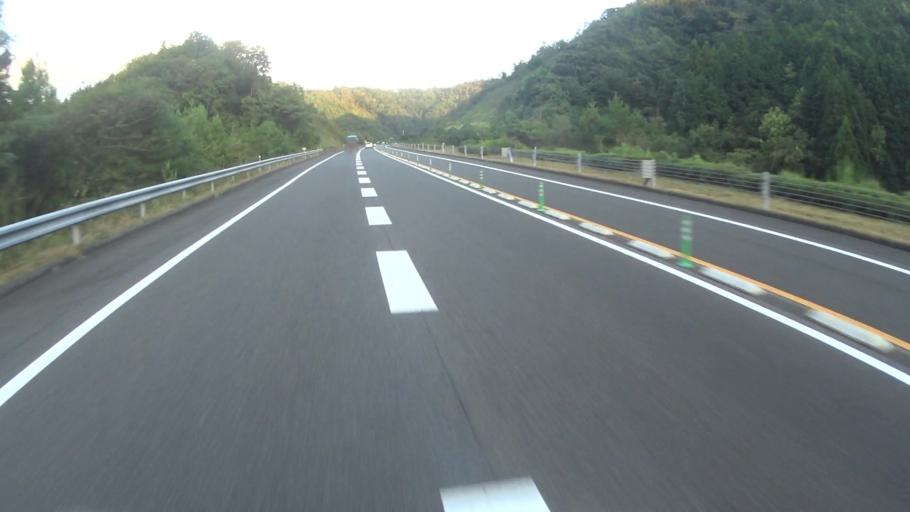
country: JP
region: Kyoto
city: Ayabe
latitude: 35.3827
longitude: 135.2497
